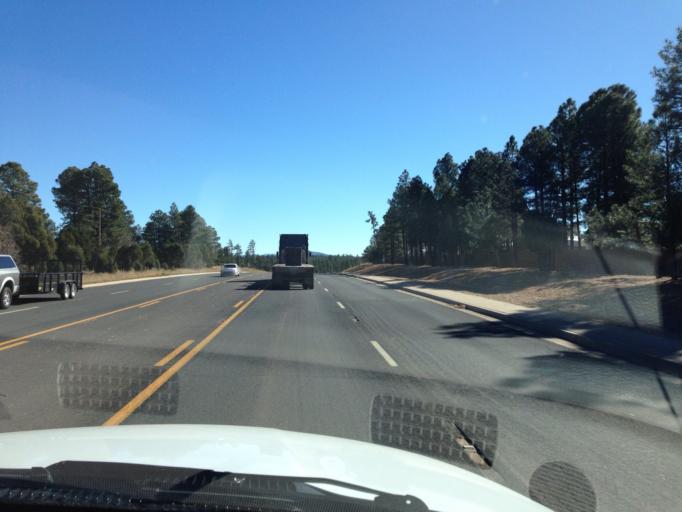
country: US
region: Arizona
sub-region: Navajo County
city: Show Low
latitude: 34.2518
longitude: -110.0794
